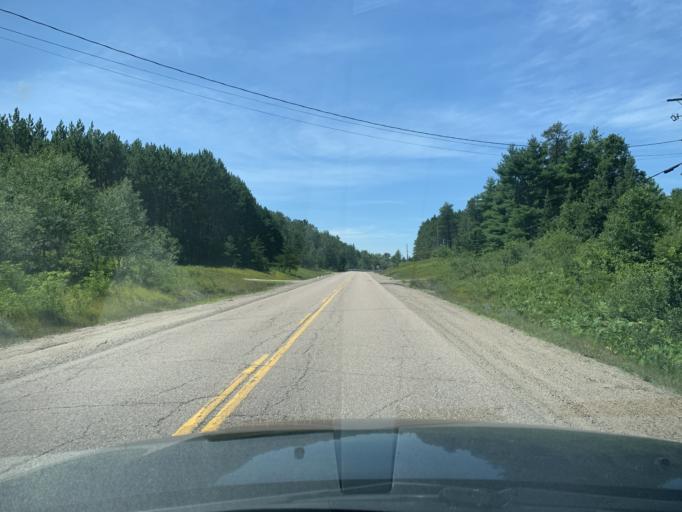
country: CA
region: Ontario
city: Petawawa
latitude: 45.6672
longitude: -77.5684
